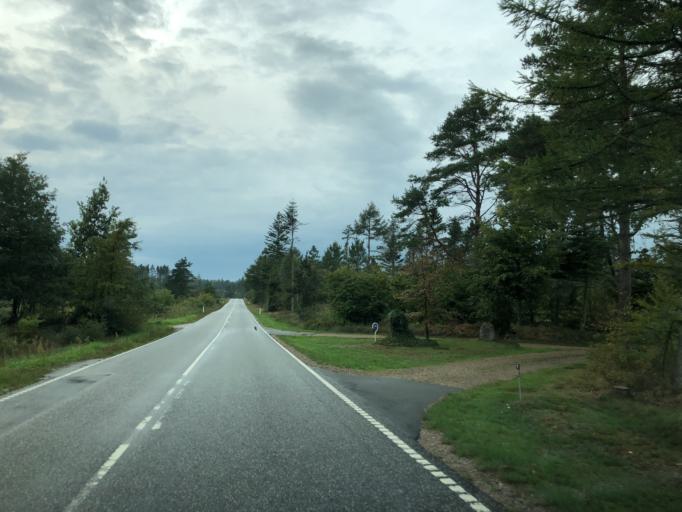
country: DK
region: Central Jutland
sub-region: Ikast-Brande Kommune
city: Brande
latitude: 56.0002
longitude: 9.1874
